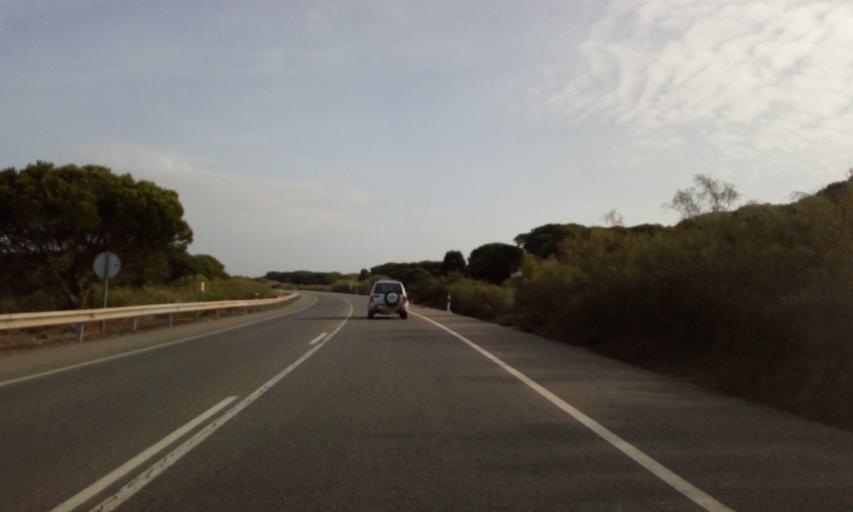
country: ES
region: Andalusia
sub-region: Provincia de Huelva
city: Palos de la Frontera
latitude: 37.1516
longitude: -6.8676
